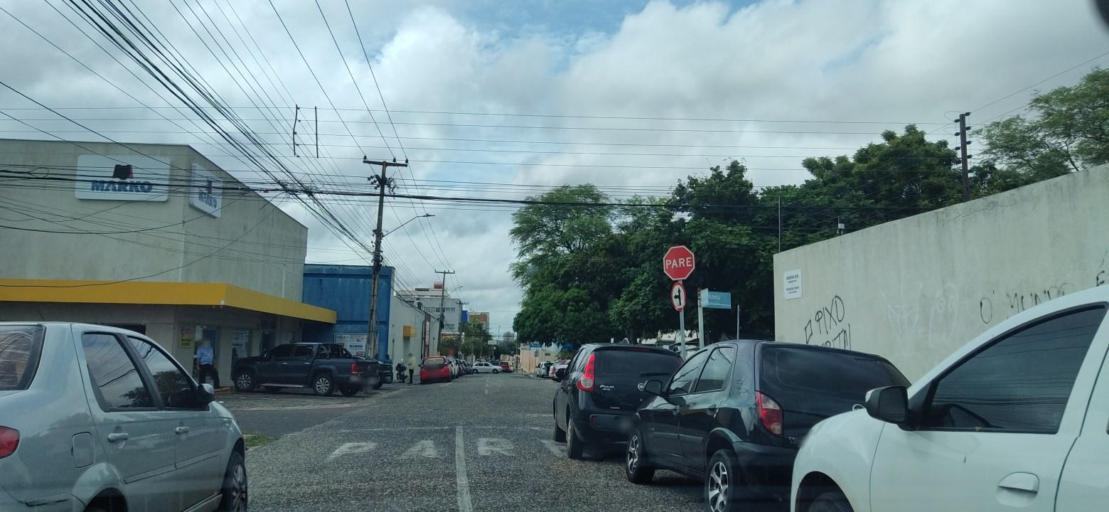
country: BR
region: Piaui
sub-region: Teresina
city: Teresina
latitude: -5.0866
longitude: -42.8099
